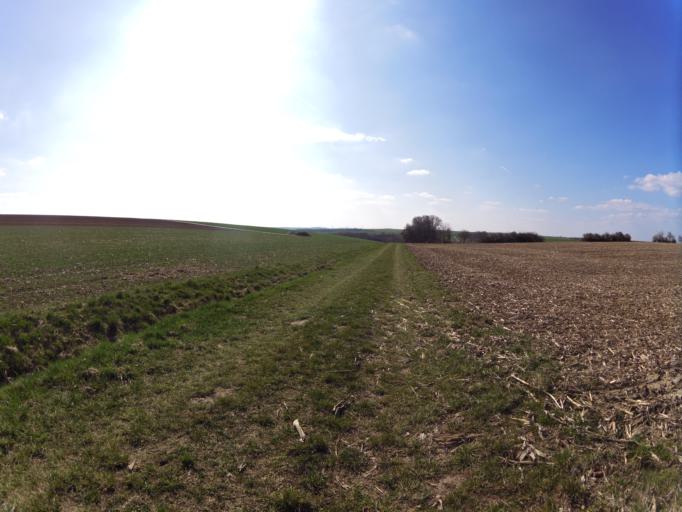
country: DE
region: Bavaria
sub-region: Regierungsbezirk Unterfranken
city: Nordheim
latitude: 49.8384
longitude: 10.1589
